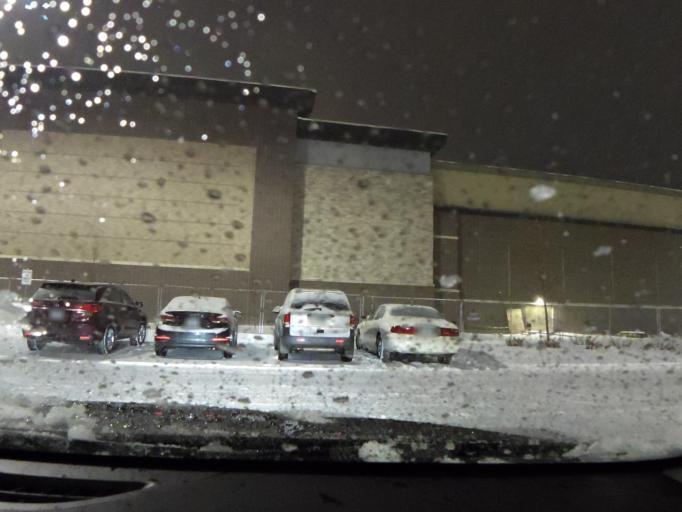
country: US
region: Minnesota
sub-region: Hennepin County
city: Eden Prairie
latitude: 44.8537
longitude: -93.4268
